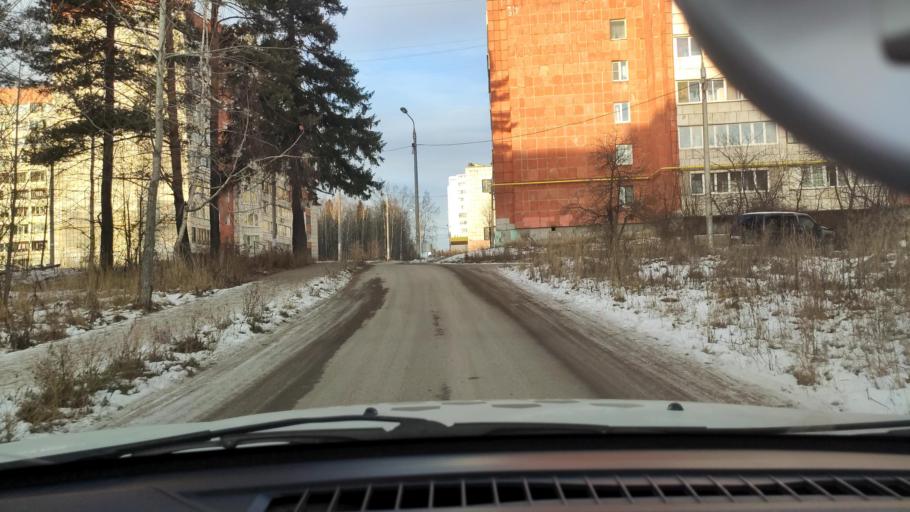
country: RU
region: Perm
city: Kondratovo
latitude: 58.0435
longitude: 56.0827
